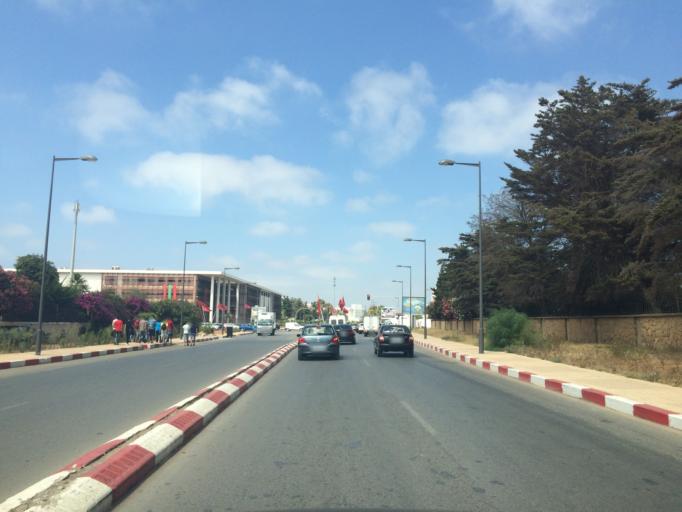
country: MA
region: Rabat-Sale-Zemmour-Zaer
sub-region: Skhirate-Temara
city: Temara
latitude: 33.9681
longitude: -6.8752
